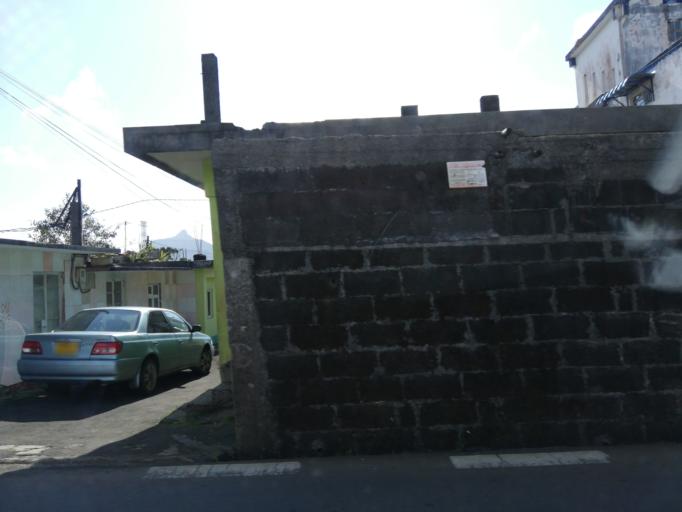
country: MU
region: Pamplemousses
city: Creve Coeur
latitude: -20.2075
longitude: 57.5668
